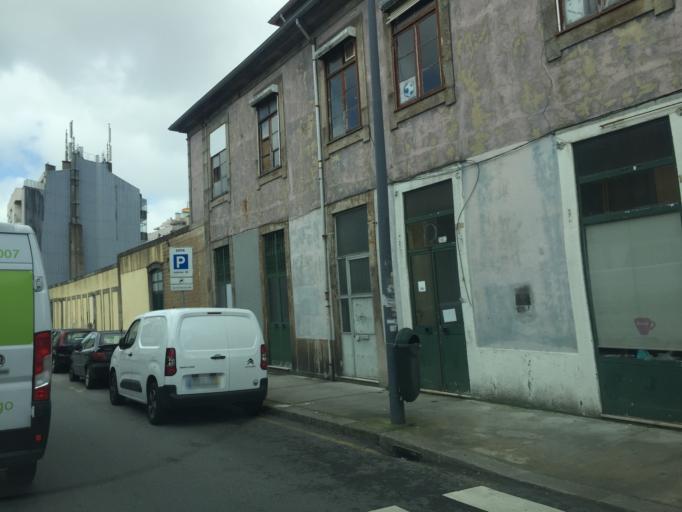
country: PT
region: Porto
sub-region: Porto
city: Porto
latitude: 41.1627
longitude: -8.6112
